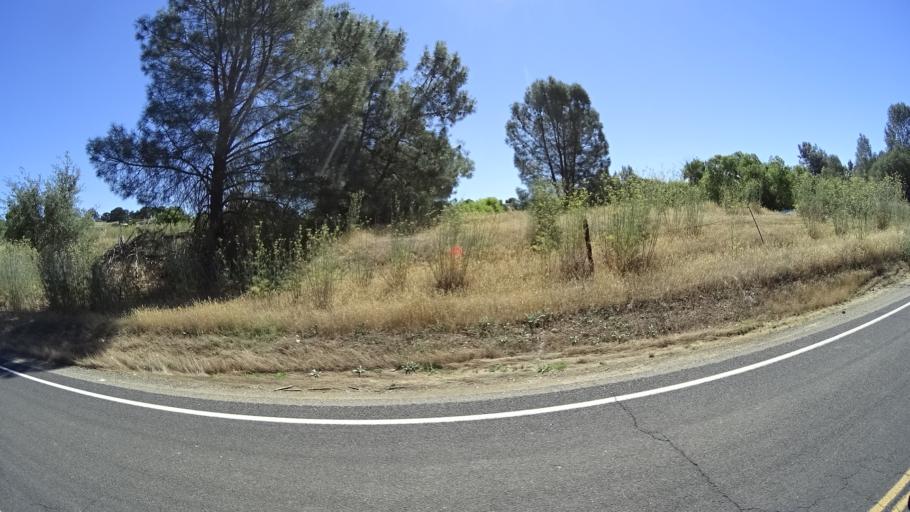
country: US
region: California
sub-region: Calaveras County
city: Rancho Calaveras
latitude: 38.0940
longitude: -120.8721
